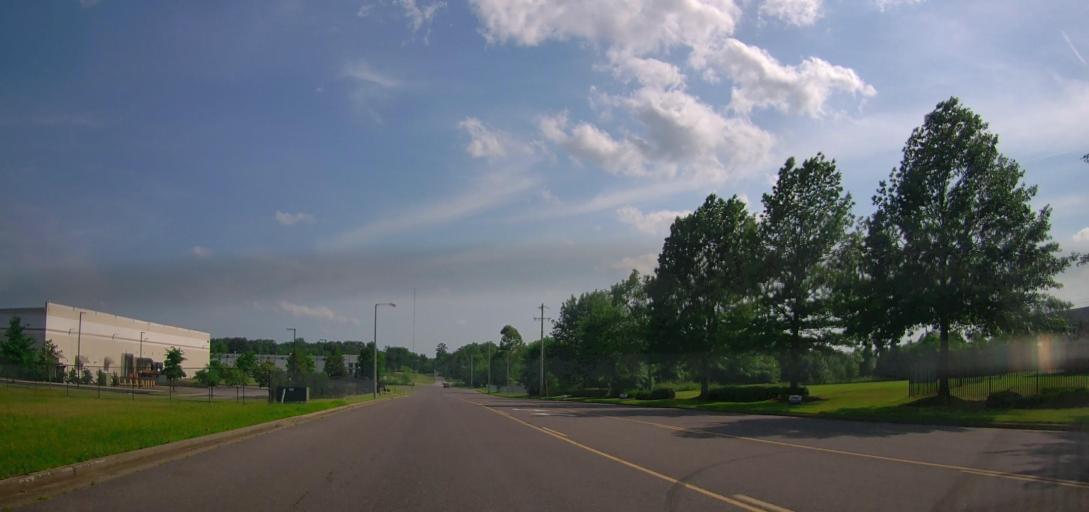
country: US
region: Mississippi
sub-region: De Soto County
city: Olive Branch
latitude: 34.9992
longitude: -89.8604
